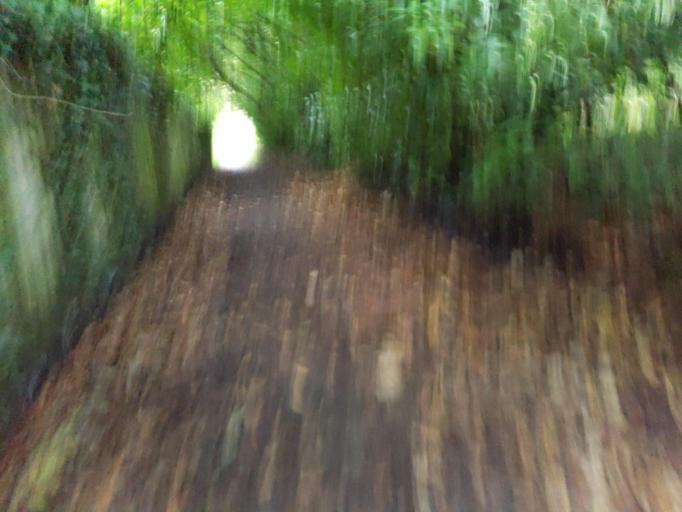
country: GB
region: England
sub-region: Cornwall
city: Saltash
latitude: 50.4265
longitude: -4.1829
